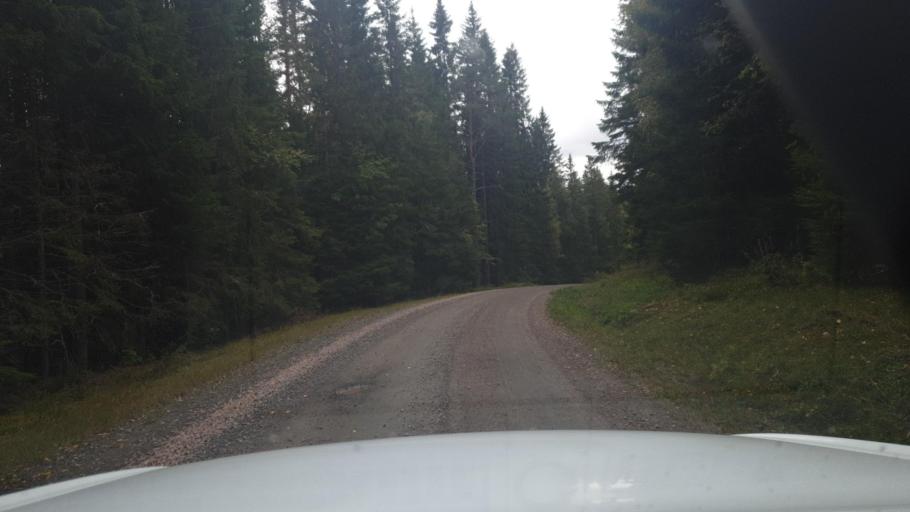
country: SE
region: Vaermland
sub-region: Eda Kommun
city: Charlottenberg
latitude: 60.1438
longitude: 12.5988
